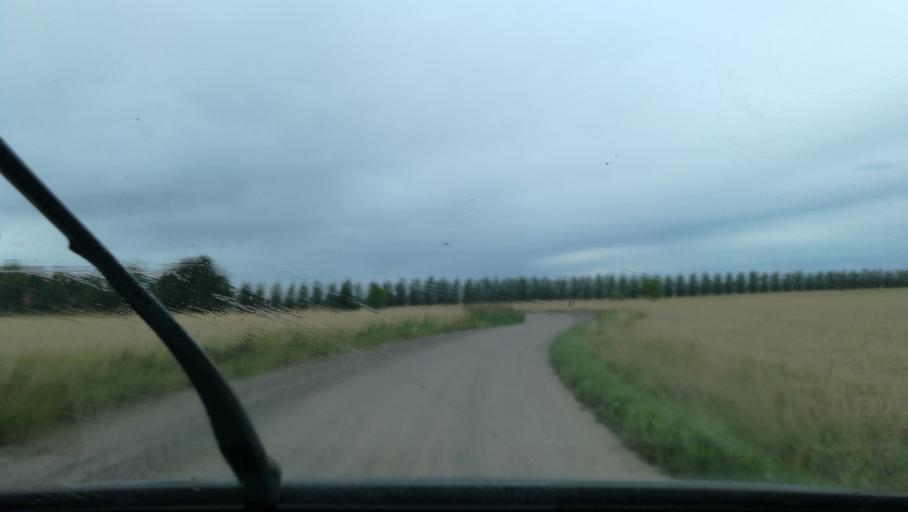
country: SE
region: Vaestmanland
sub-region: Vasteras
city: Tillberga
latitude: 59.7158
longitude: 16.6137
